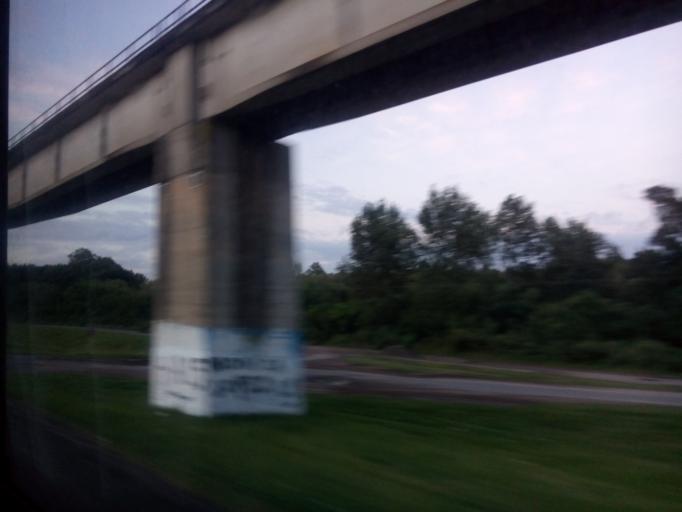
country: AR
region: Buenos Aires
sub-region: Partido de Zarate
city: Zarate
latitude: -34.0825
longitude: -58.9965
